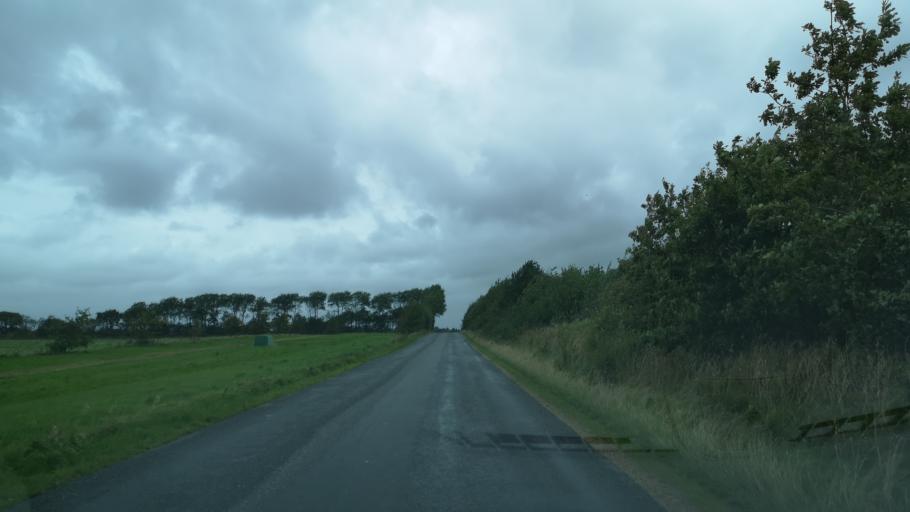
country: DK
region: Central Jutland
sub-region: Ringkobing-Skjern Kommune
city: Videbaek
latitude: 56.0614
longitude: 8.6731
